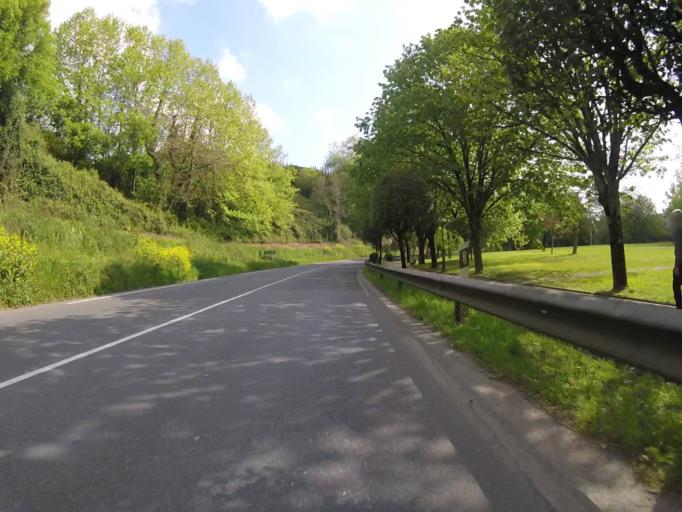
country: ES
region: Basque Country
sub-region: Provincia de Guipuzcoa
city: Azkoitia
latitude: 43.1744
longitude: -2.3003
